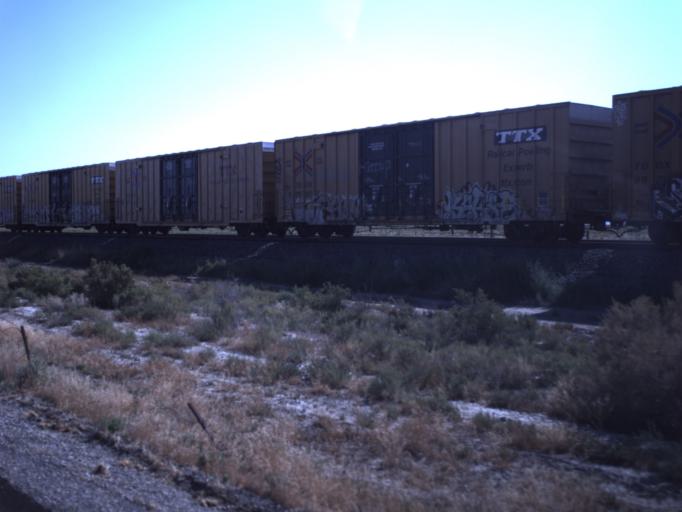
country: US
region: Utah
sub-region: Millard County
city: Delta
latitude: 39.2298
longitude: -112.6694
